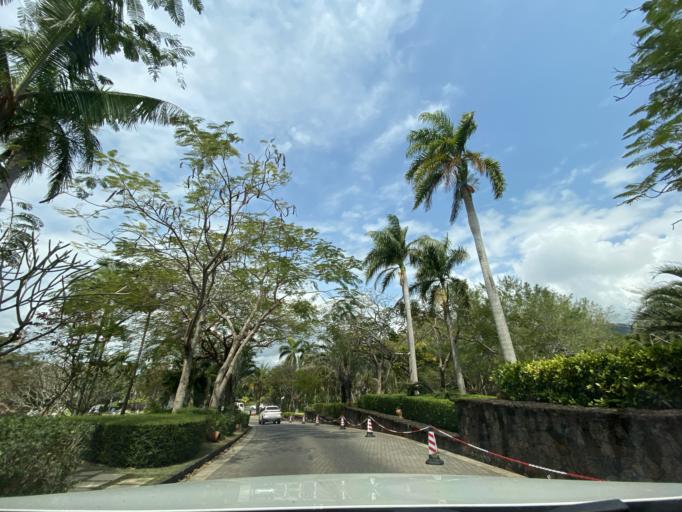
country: CN
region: Hainan
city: Tiandu
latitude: 18.2302
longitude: 109.6292
